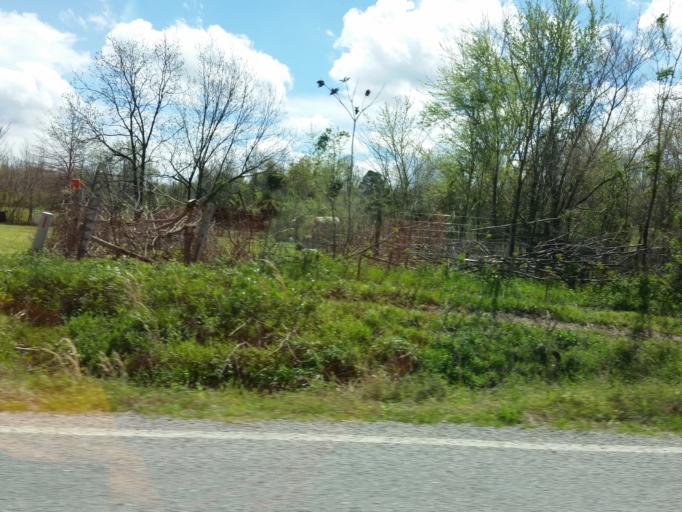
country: US
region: Arkansas
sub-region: Craighead County
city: Bono
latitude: 36.0119
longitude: -90.6999
